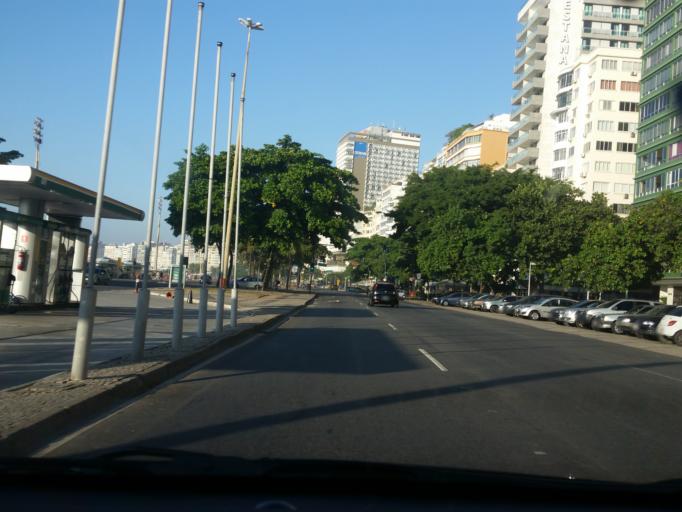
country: BR
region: Rio de Janeiro
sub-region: Rio De Janeiro
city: Rio de Janeiro
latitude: -22.9741
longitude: -43.1868
